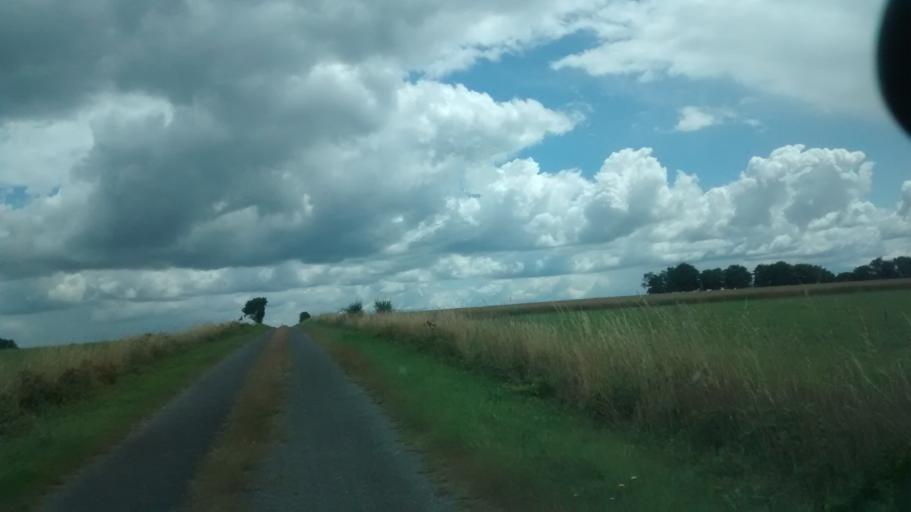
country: FR
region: Brittany
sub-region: Departement d'Ille-et-Vilaine
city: La Dominelais
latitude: 47.7868
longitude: -1.7233
